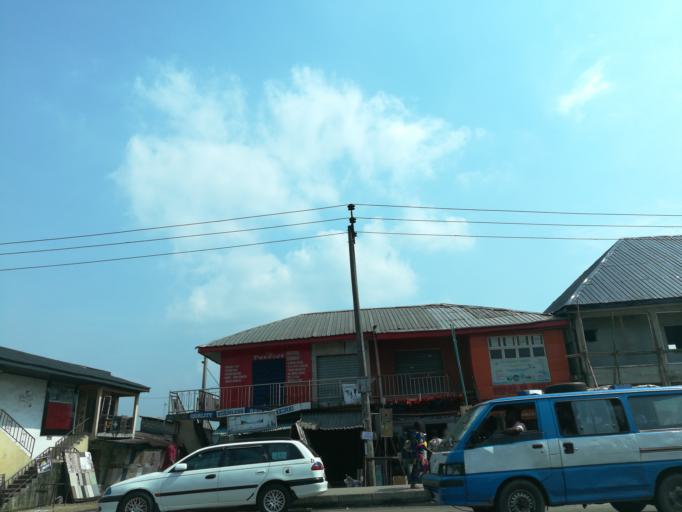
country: NG
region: Rivers
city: Port Harcourt
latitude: 4.8079
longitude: 6.9862
